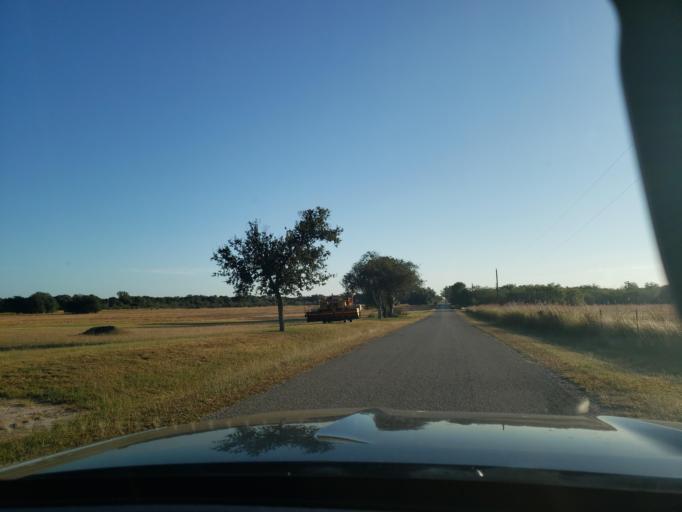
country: US
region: Texas
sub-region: Bee County
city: Beeville
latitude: 28.4211
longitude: -97.7108
